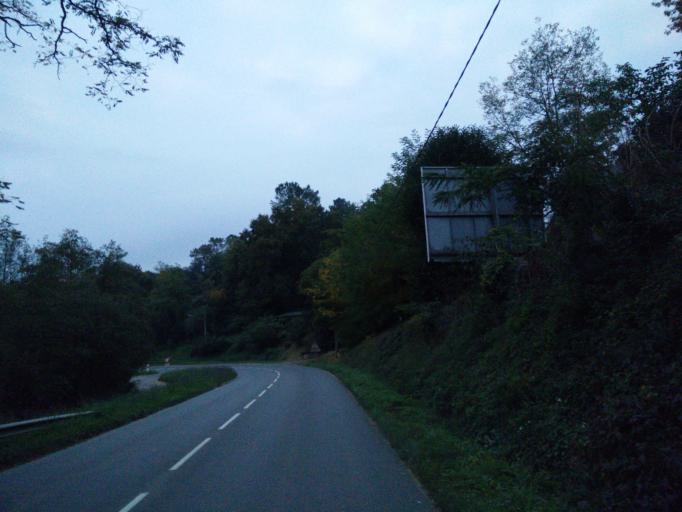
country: FR
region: Aquitaine
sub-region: Departement de la Dordogne
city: Sarlat-la-Caneda
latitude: 44.8738
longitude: 1.2371
